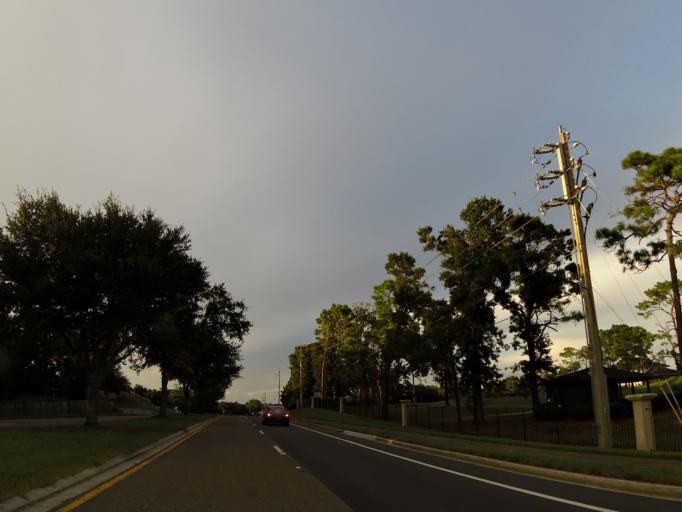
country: US
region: Florida
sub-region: Duval County
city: Atlantic Beach
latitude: 30.3685
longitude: -81.5029
